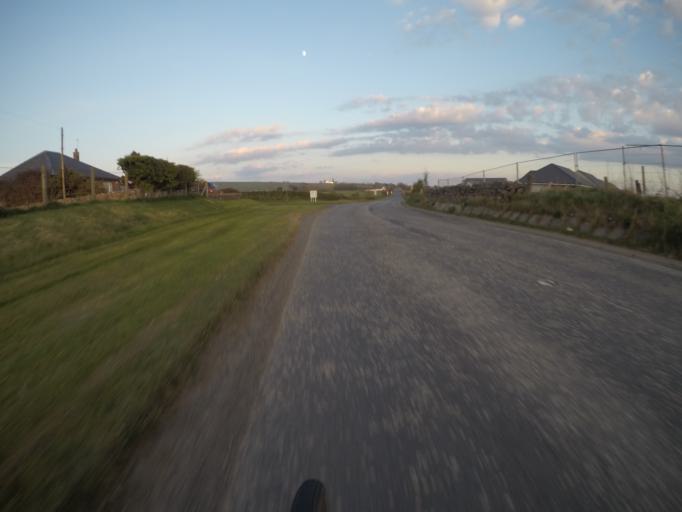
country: GB
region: Scotland
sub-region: South Ayrshire
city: Troon
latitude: 55.5627
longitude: -4.6343
